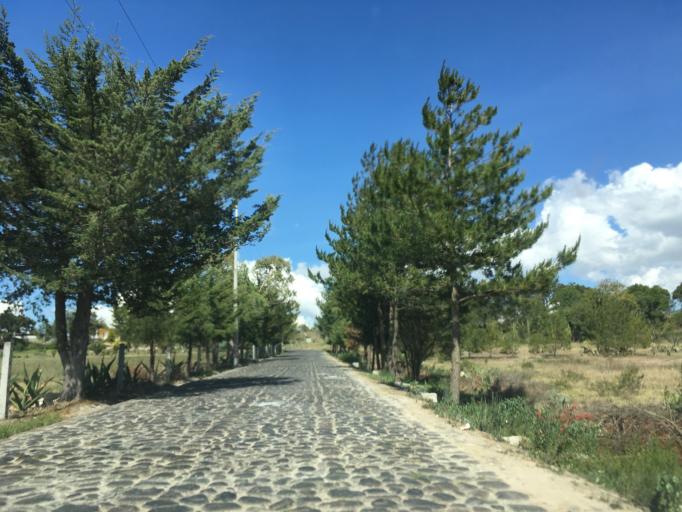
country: MX
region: Hidalgo
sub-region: Omitlan de Juarez
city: San Antonio el Paso
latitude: 20.2322
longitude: -98.5570
